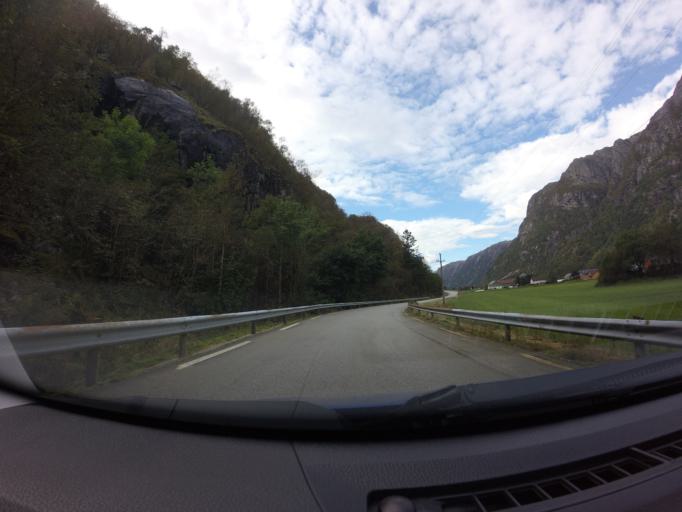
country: NO
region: Rogaland
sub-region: Forsand
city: Forsand
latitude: 58.8412
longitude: 6.3147
